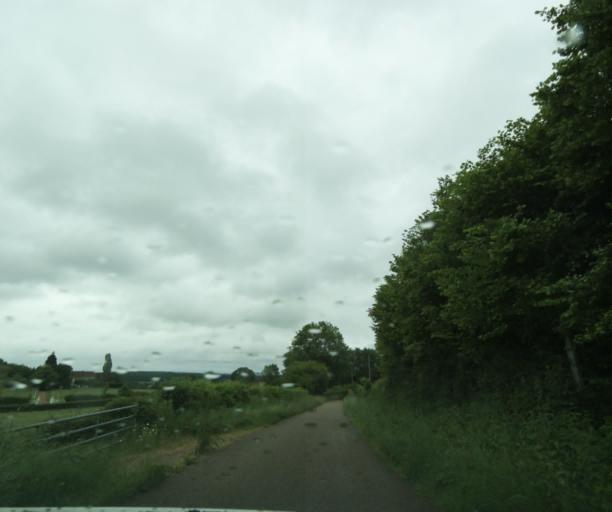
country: FR
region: Bourgogne
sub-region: Departement de Saone-et-Loire
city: Charolles
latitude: 46.4882
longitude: 4.2685
